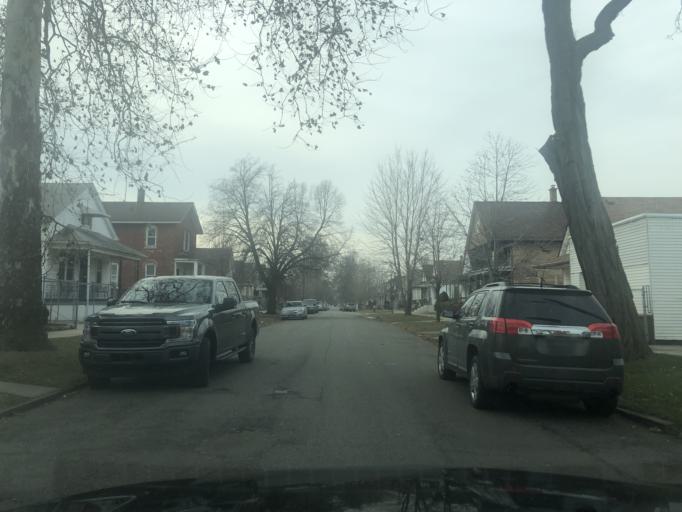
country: US
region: Michigan
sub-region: Wayne County
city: Detroit
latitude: 42.3239
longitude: -83.1020
